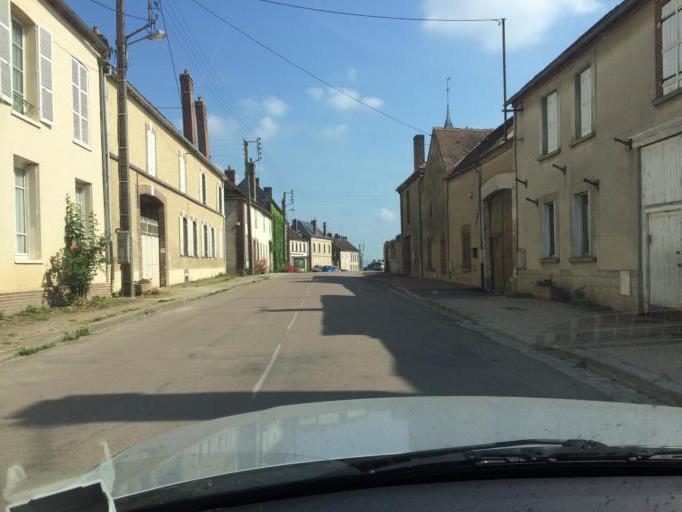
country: FR
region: Bourgogne
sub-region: Departement de l'Yonne
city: Fleury-la-Vallee
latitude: 47.9157
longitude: 3.4384
